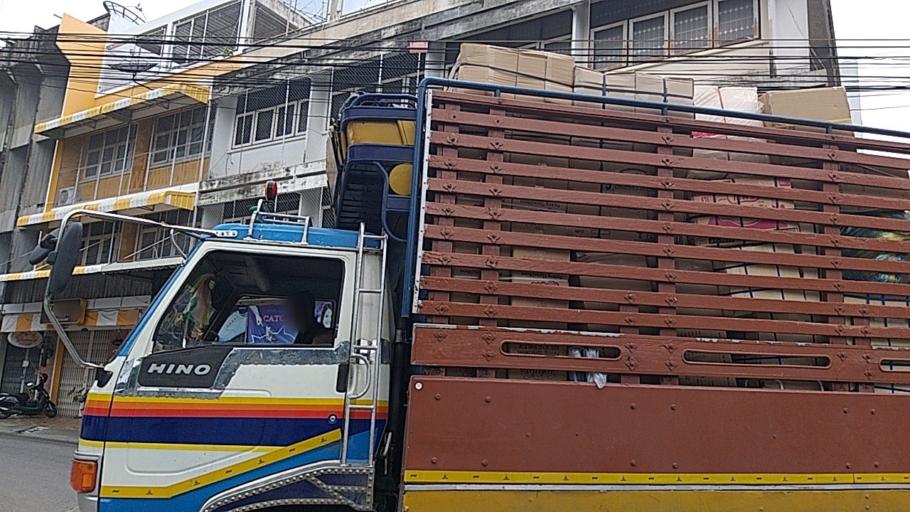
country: TH
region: Nakhon Pathom
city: Nakhon Pathom
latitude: 13.8210
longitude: 100.0568
